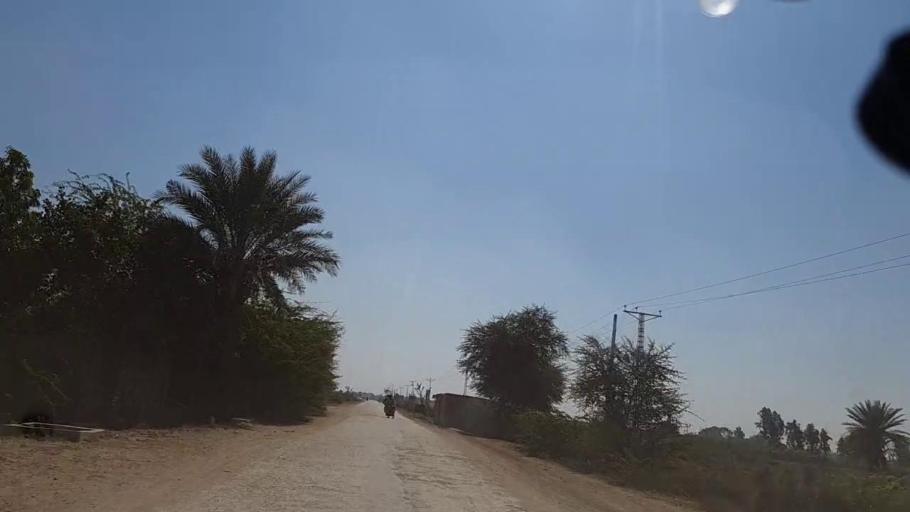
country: PK
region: Sindh
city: Mirpur Khas
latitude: 25.4981
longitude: 69.0360
